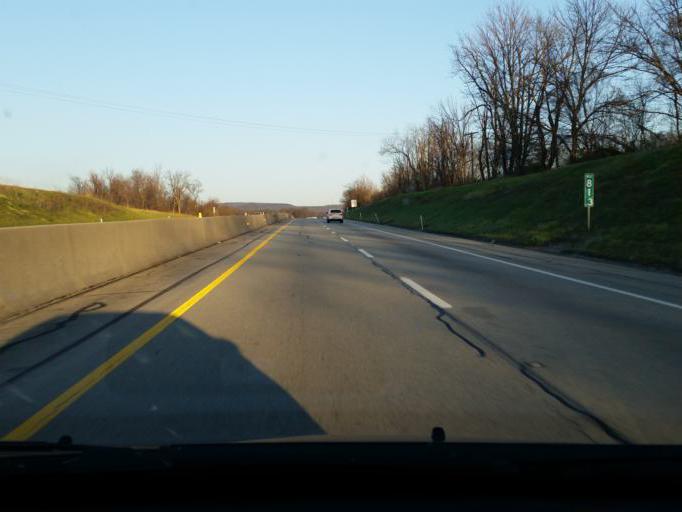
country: US
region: Pennsylvania
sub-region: Westmoreland County
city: Mount Pleasant
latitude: 40.1769
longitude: -79.5136
